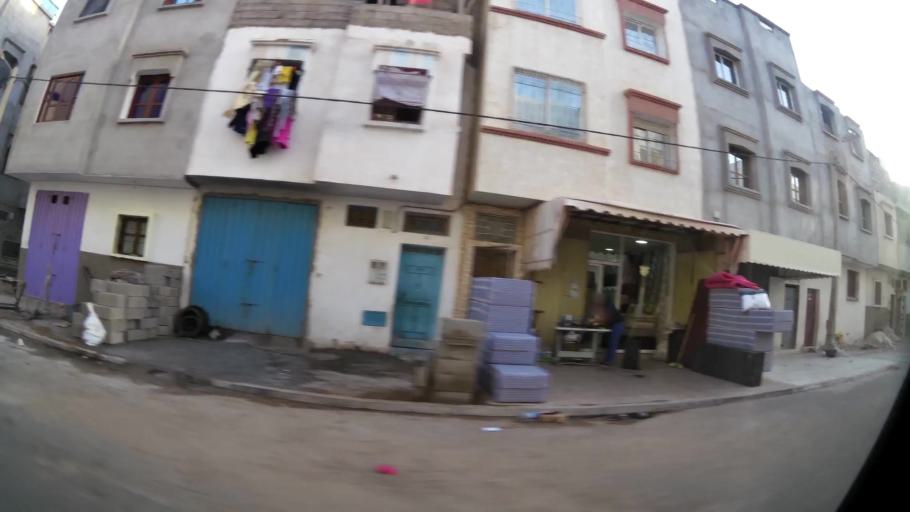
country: MA
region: Oued ed Dahab-Lagouira
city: Dakhla
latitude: 30.3979
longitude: -9.5604
